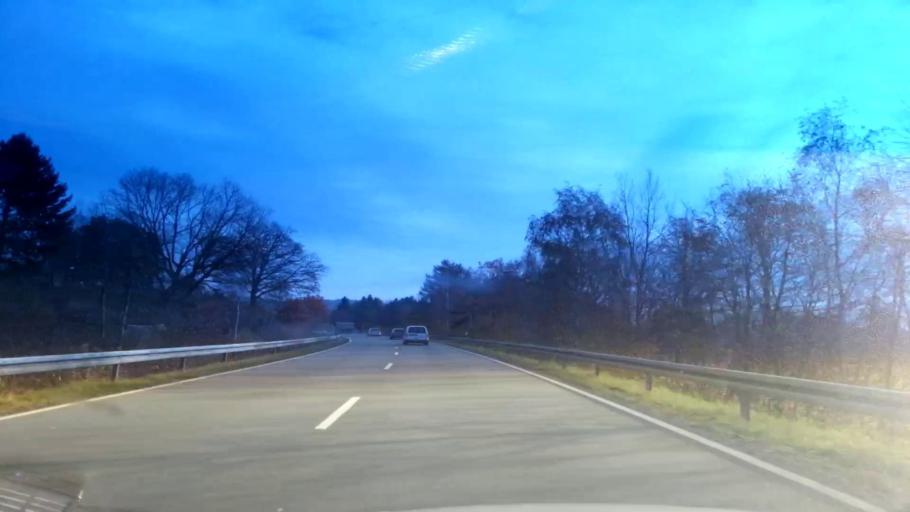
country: DE
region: Bavaria
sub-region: Upper Franconia
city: Seybothenreuth
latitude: 49.9452
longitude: 11.7253
